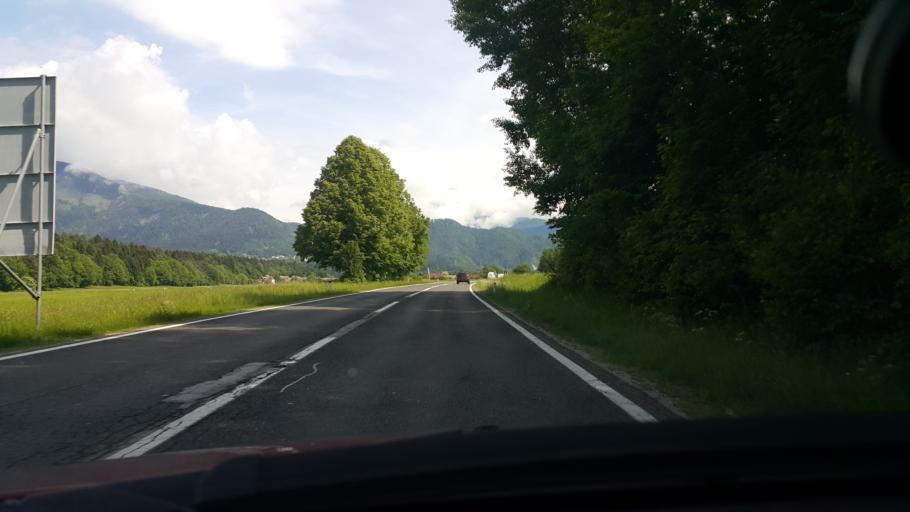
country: SI
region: Trzic
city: Bistrica pri Trzicu
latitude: 46.3222
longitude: 14.2787
